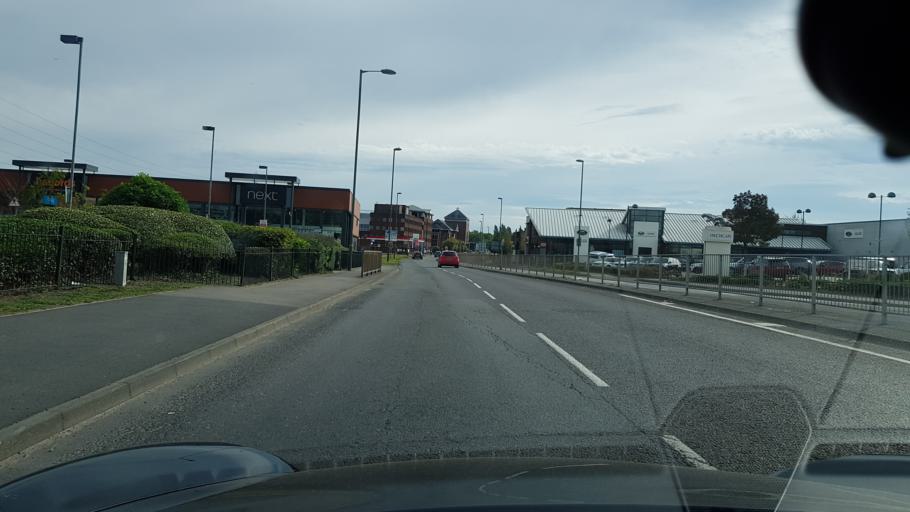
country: GB
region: England
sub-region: Surrey
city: Guildford
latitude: 51.2479
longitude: -0.5791
